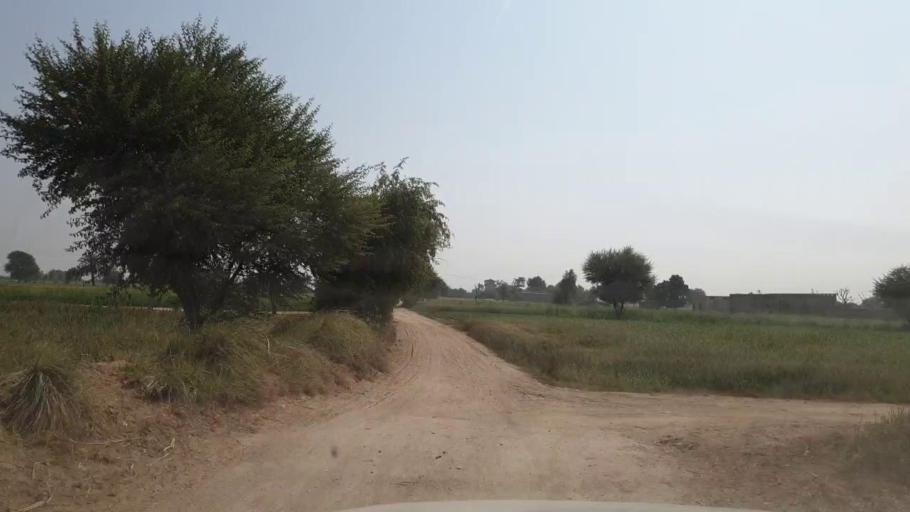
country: PK
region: Sindh
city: Mirpur Khas
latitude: 25.6467
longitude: 69.1156
